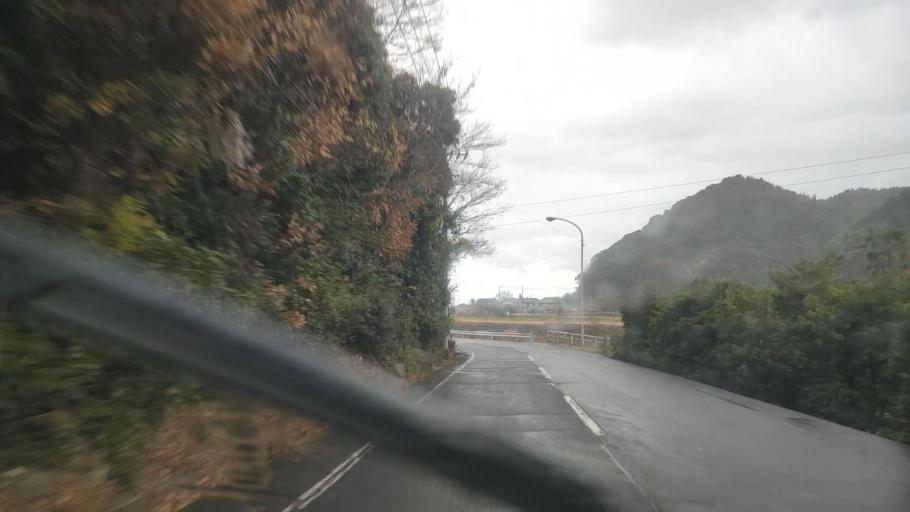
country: JP
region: Tokushima
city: Ishii
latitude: 34.2009
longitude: 134.4013
